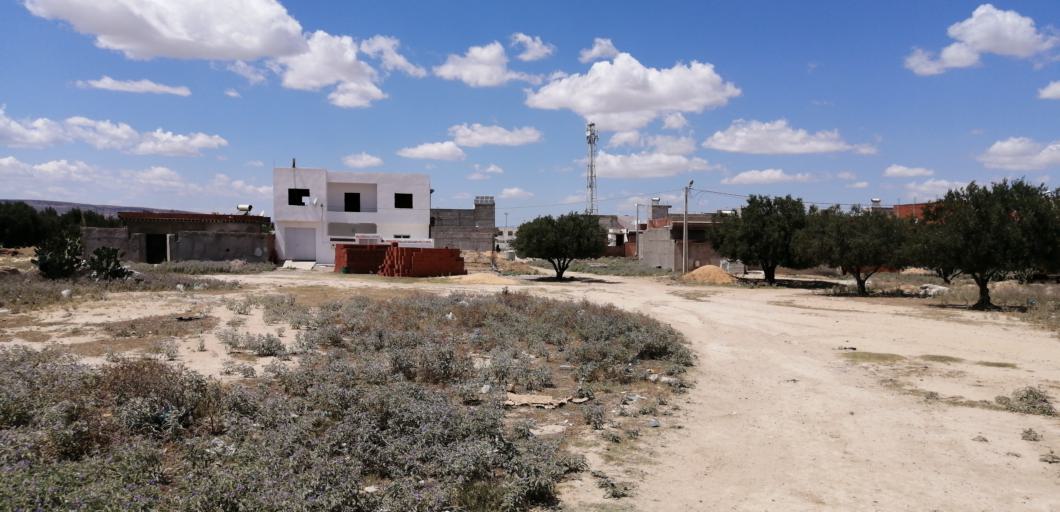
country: TN
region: Al Qayrawan
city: Kairouan
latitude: 35.6155
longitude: 9.9241
